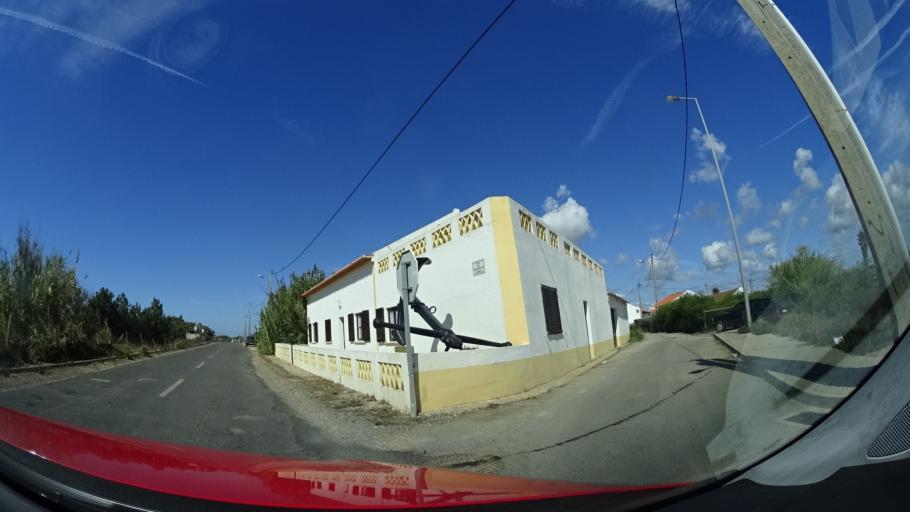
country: PT
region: Beja
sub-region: Odemira
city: Sao Teotonio
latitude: 37.5281
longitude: -8.7843
